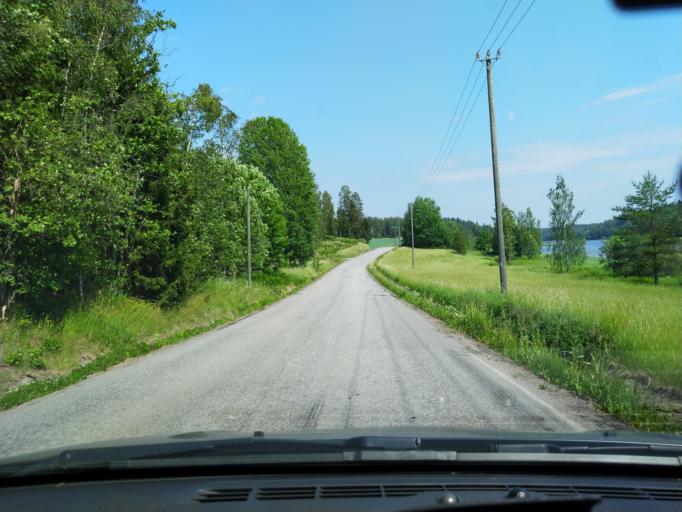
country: FI
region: Uusimaa
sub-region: Helsinki
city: Lohja
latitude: 60.3451
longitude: 24.0870
